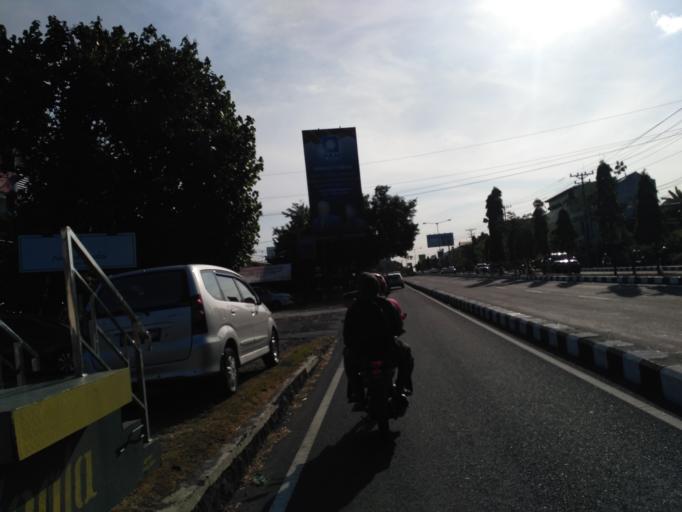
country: ID
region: Daerah Istimewa Yogyakarta
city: Depok
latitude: -7.7626
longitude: 110.4155
